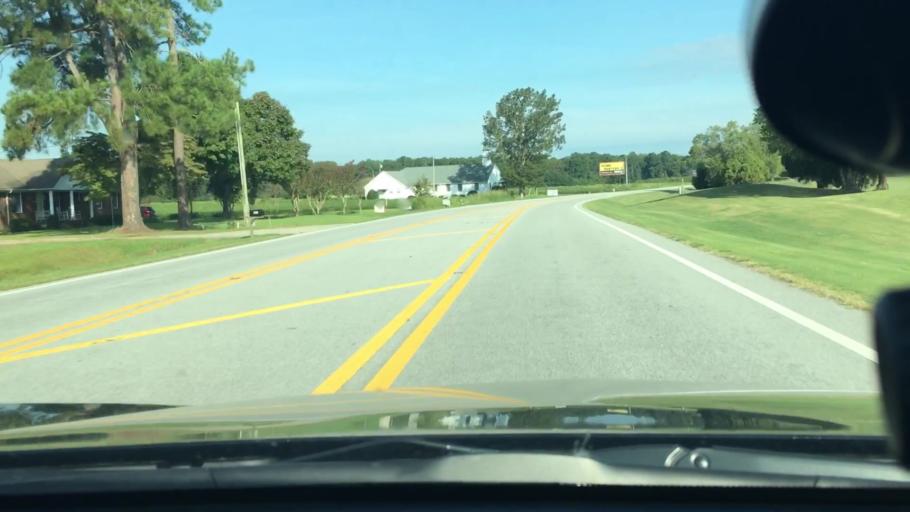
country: US
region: North Carolina
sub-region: Pitt County
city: Summerfield
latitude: 35.6356
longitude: -77.4477
